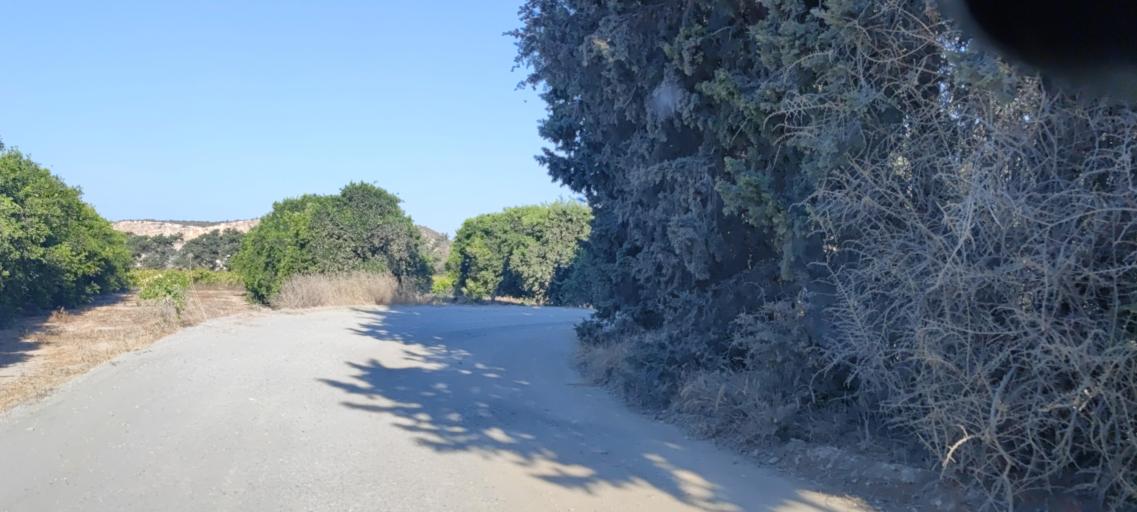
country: CY
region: Limassol
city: Sotira
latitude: 34.6646
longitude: 32.8008
